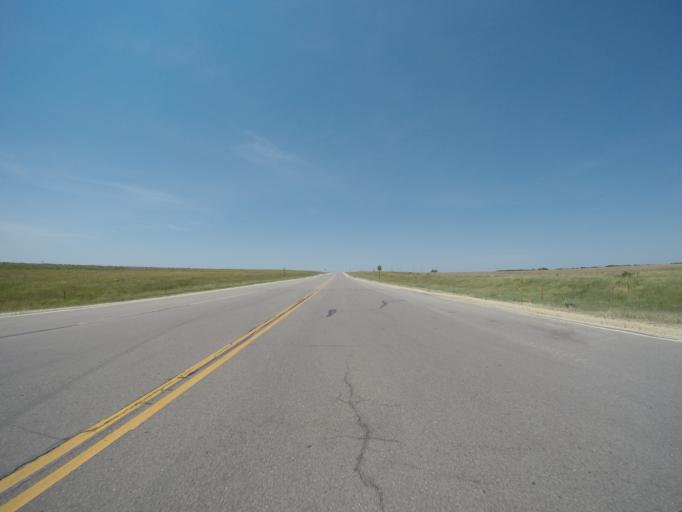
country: US
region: Kansas
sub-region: Ottawa County
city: Minneapolis
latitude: 39.1027
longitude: -97.6481
